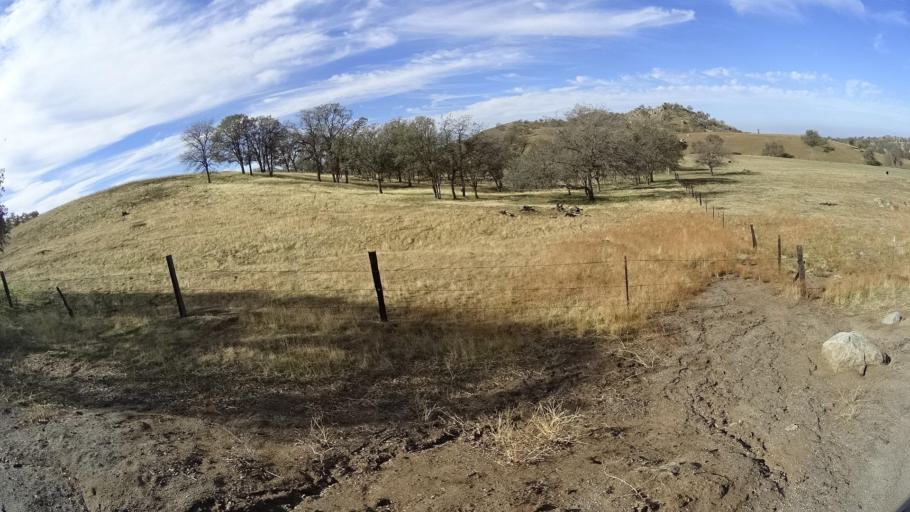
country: US
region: California
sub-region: Kern County
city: Oildale
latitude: 35.5772
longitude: -118.8116
